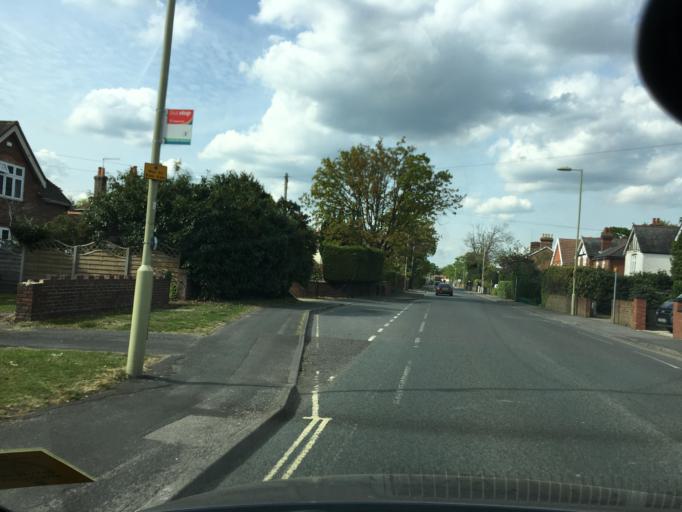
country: GB
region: England
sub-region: Hampshire
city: Farnborough
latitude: 51.2977
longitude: -0.7776
